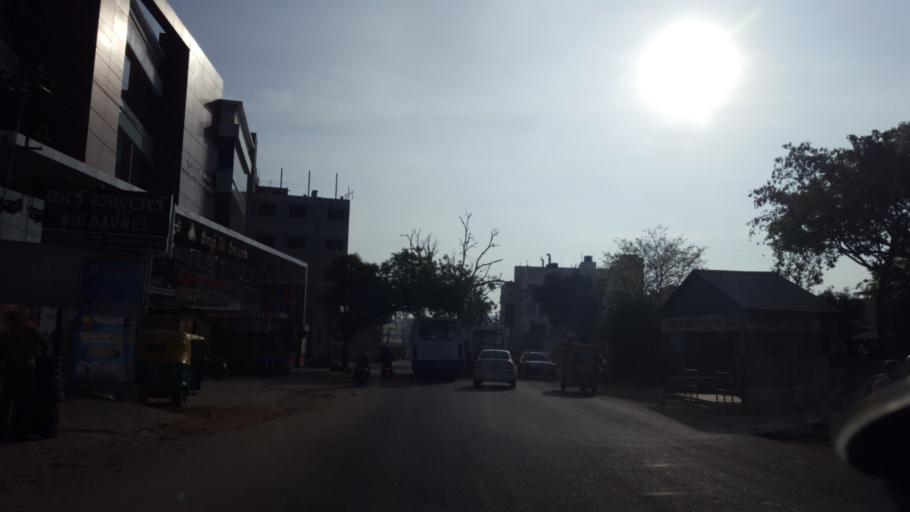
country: IN
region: Karnataka
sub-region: Bangalore Urban
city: Bangalore
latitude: 12.9039
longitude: 77.5076
